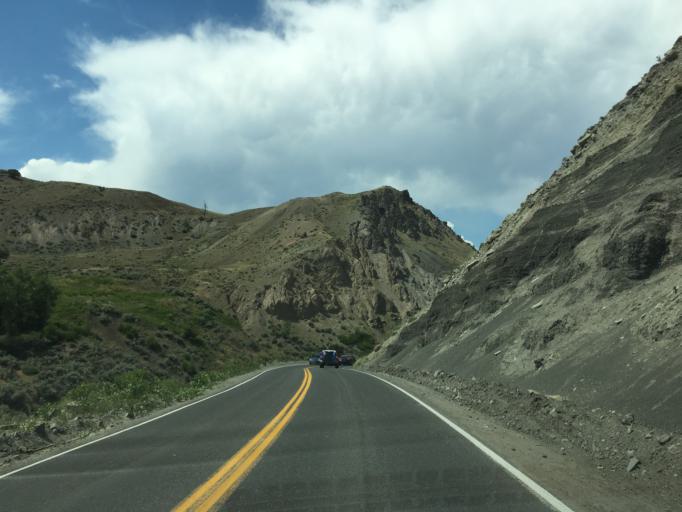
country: US
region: Montana
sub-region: Gallatin County
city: West Yellowstone
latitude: 45.0072
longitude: -110.6938
